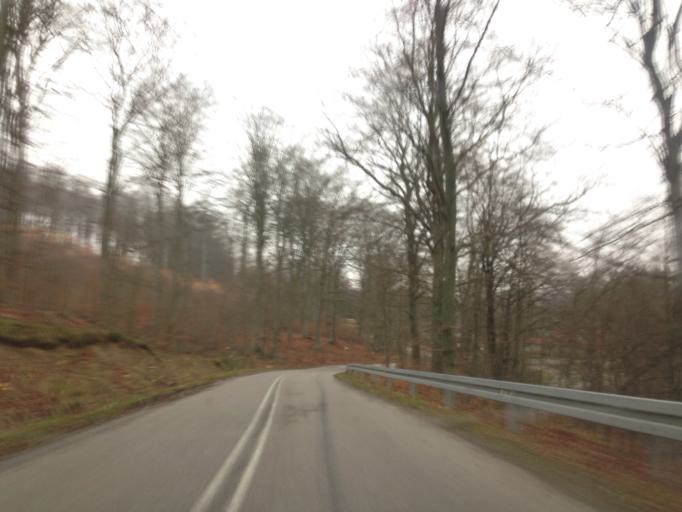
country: PL
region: Pomeranian Voivodeship
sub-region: Powiat gdanski
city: Przywidz
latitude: 54.1953
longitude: 18.3330
